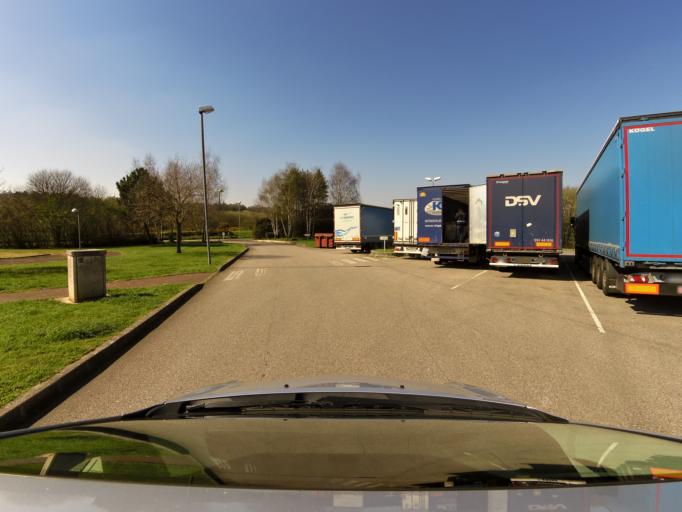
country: FR
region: Brittany
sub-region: Departement du Morbihan
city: Ploermel
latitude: 47.9198
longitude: -2.3654
